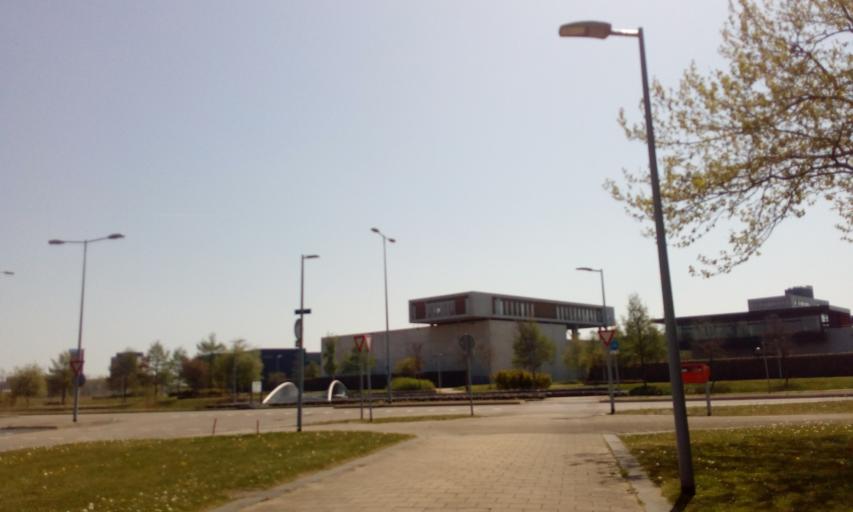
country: NL
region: South Holland
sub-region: Gemeente Kaag en Braassem
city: Oude Wetering
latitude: 52.2548
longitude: 4.6277
